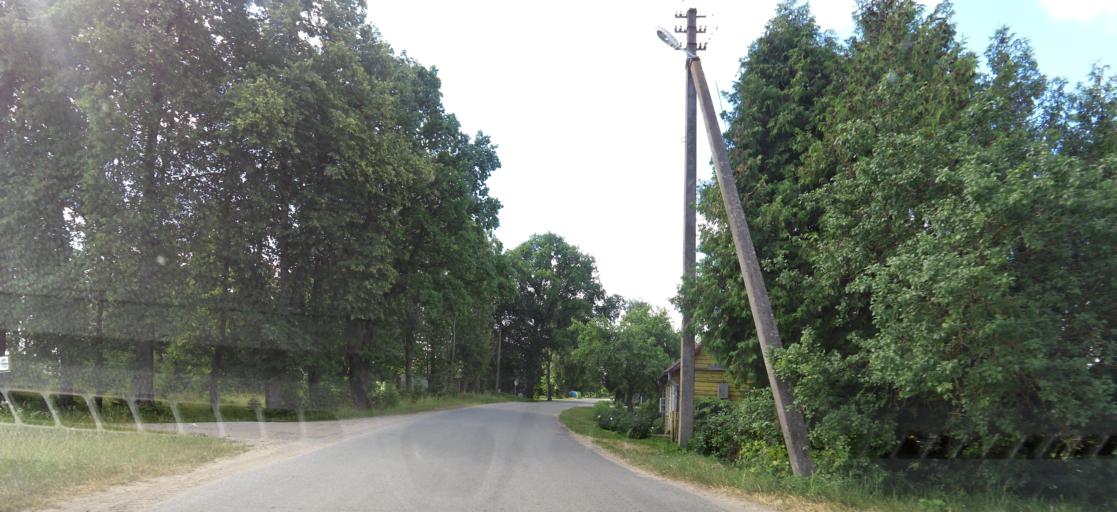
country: LT
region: Panevezys
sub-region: Birzai
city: Birzai
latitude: 56.1103
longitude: 24.8111
